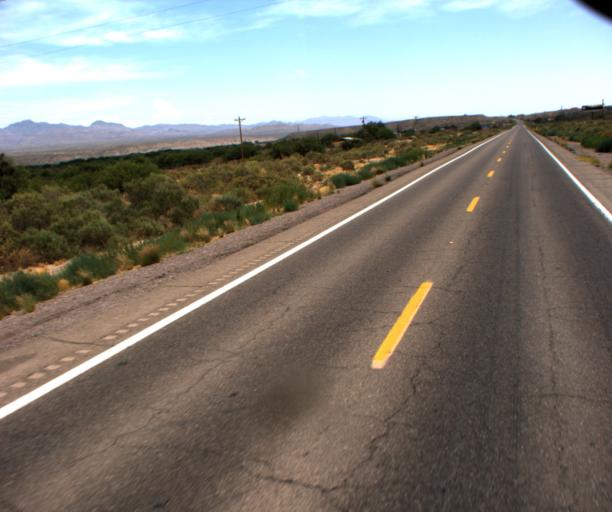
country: US
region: Arizona
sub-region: Graham County
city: Bylas
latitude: 33.0889
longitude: -110.0613
